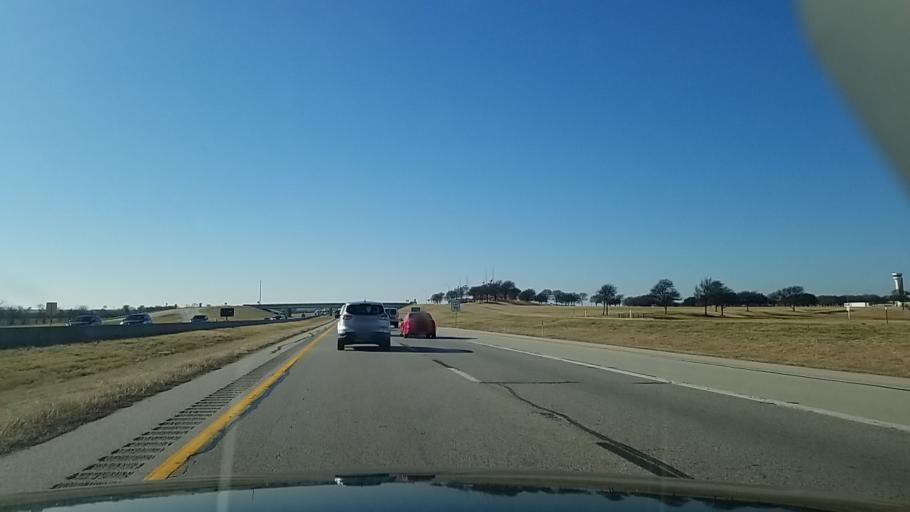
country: US
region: Texas
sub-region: Tarrant County
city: Haslet
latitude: 32.9898
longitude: -97.3007
